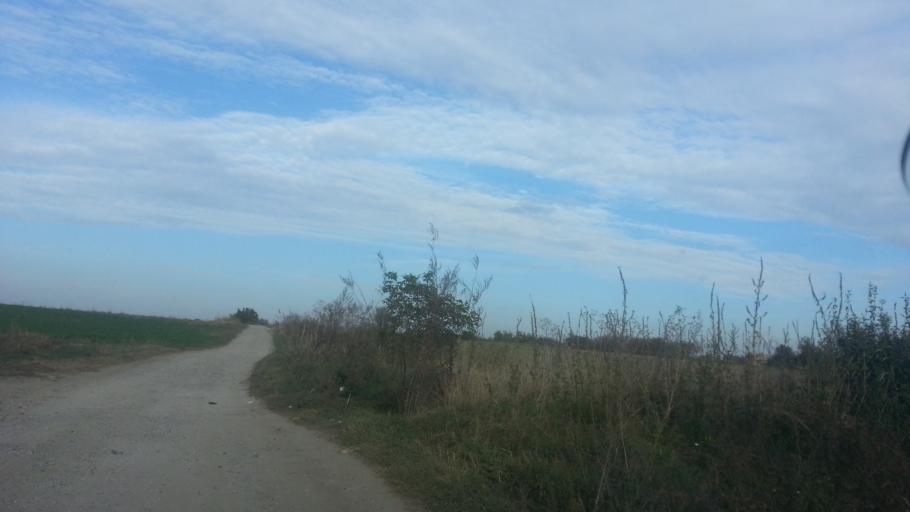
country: RS
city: Belegis
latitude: 45.0270
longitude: 20.3448
